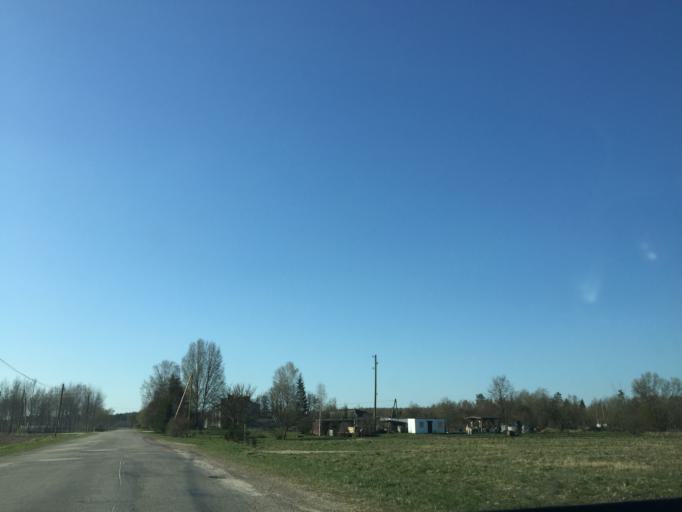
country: LV
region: Ropazu
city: Ropazi
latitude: 56.9610
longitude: 24.6898
